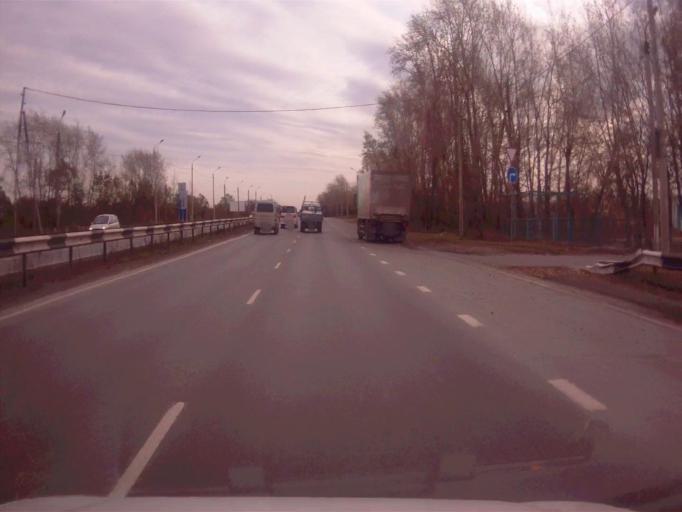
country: RU
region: Chelyabinsk
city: Novosineglazovskiy
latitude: 55.0549
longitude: 61.4080
